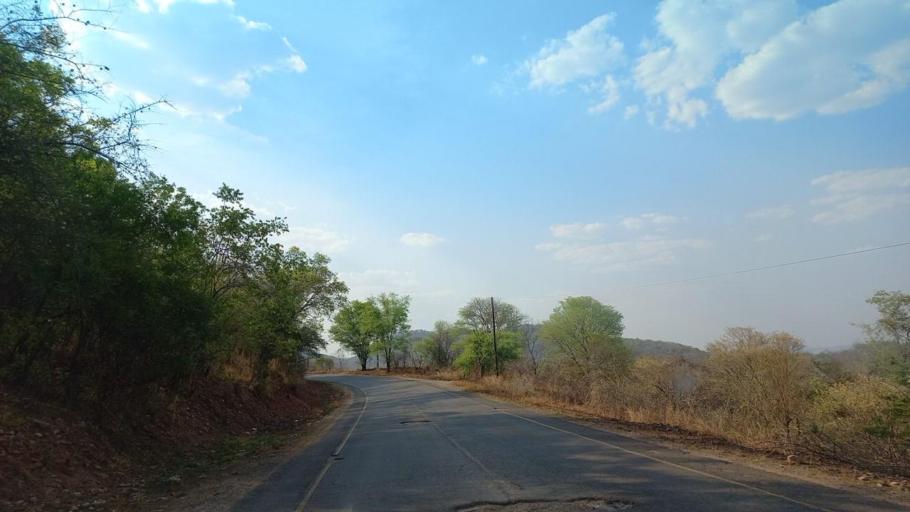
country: ZM
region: Lusaka
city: Luangwa
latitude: -14.9837
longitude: 30.1845
